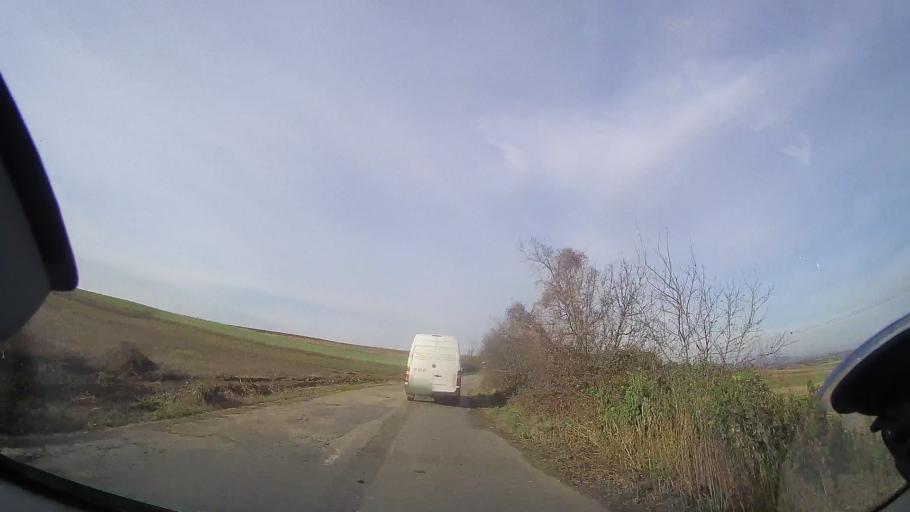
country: RO
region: Bihor
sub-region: Comuna Spinus
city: Spinus
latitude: 47.2069
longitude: 22.1814
